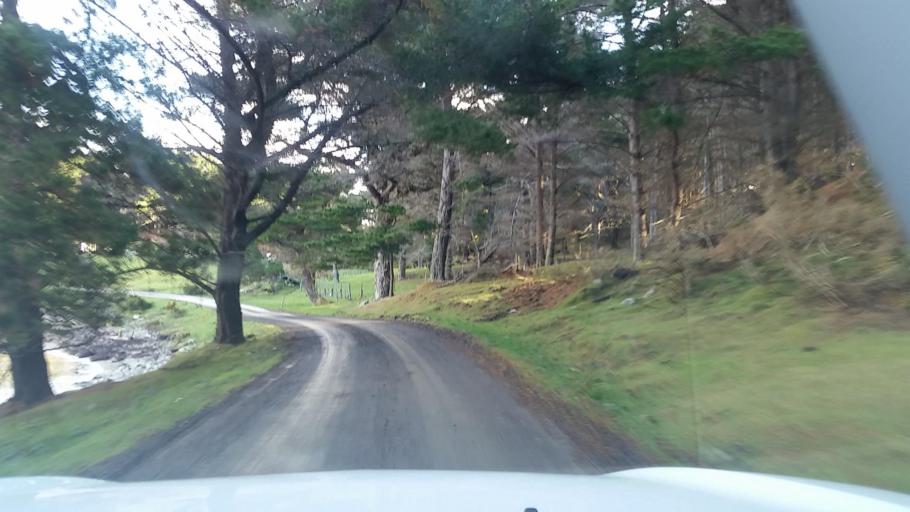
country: NZ
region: Chatham Islands
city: Waitangi
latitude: -43.8132
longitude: -176.7094
